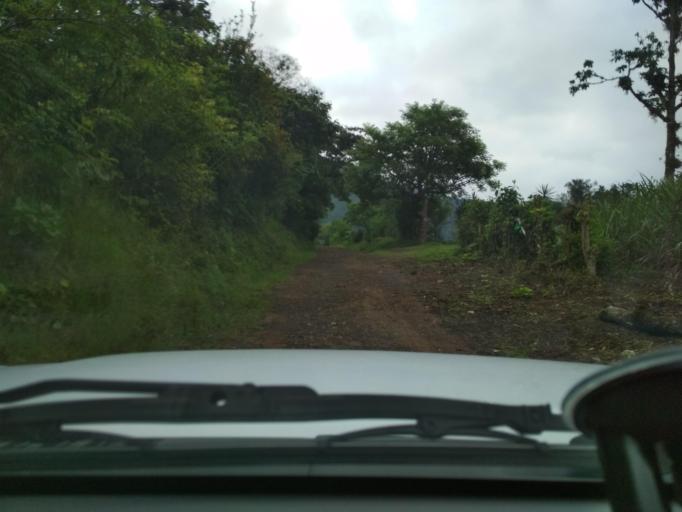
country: MX
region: Veracruz
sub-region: Ixtaczoquitlan
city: Buenavista
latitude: 18.9224
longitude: -97.0466
